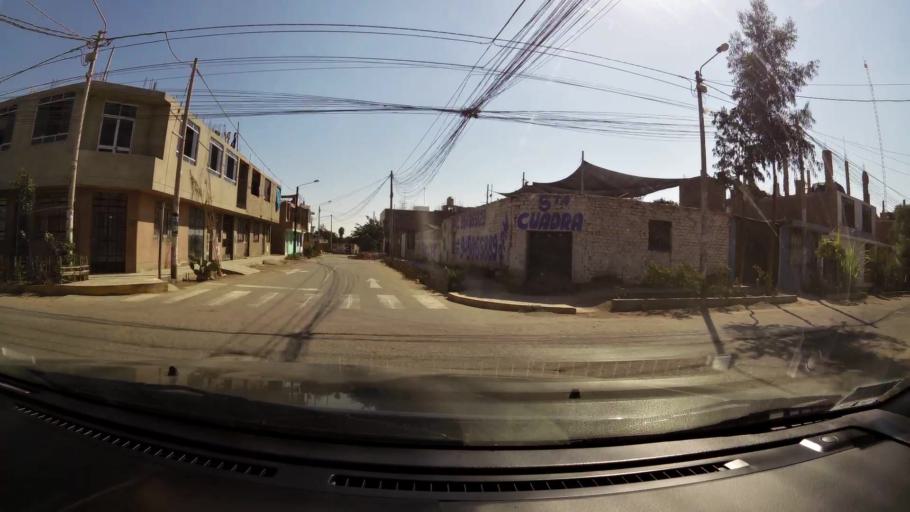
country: PE
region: Ica
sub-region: Provincia de Ica
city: La Tinguina
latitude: -14.0357
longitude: -75.7117
